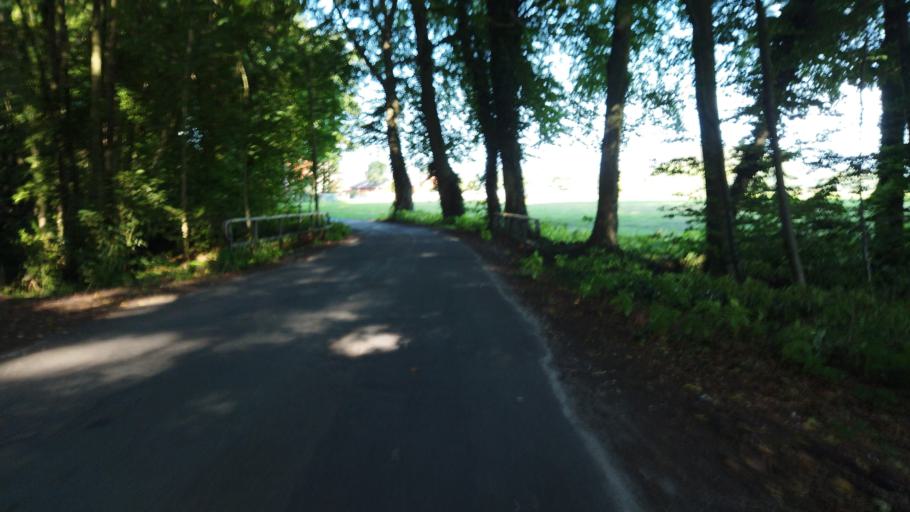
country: DE
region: Lower Saxony
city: Bad Laer
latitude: 52.1190
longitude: 8.0685
